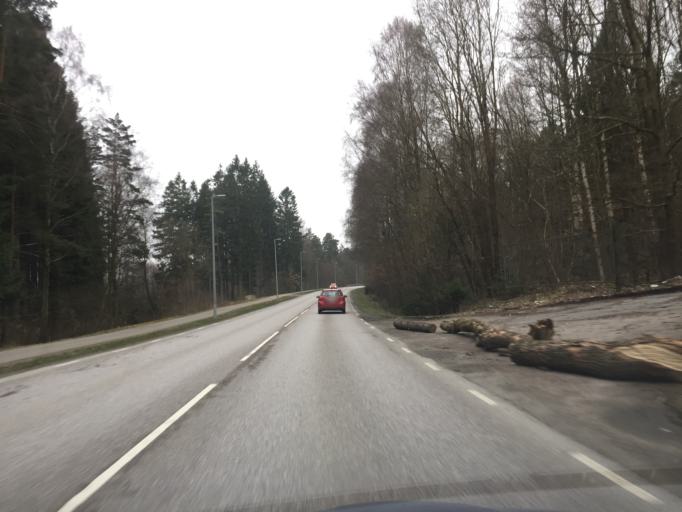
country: SE
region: Vaestra Goetaland
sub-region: Goteborg
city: Eriksbo
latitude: 57.7680
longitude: 12.0752
